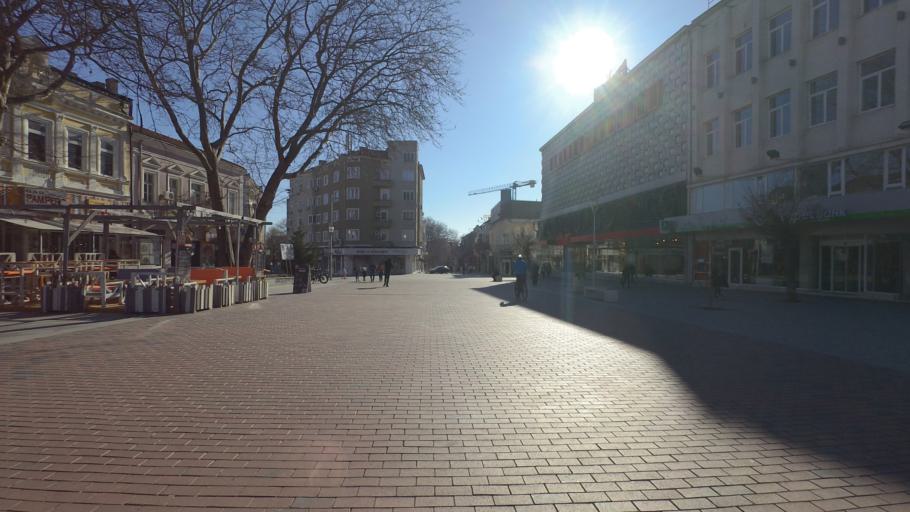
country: BG
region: Varna
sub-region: Obshtina Varna
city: Varna
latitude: 43.2033
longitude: 27.9130
